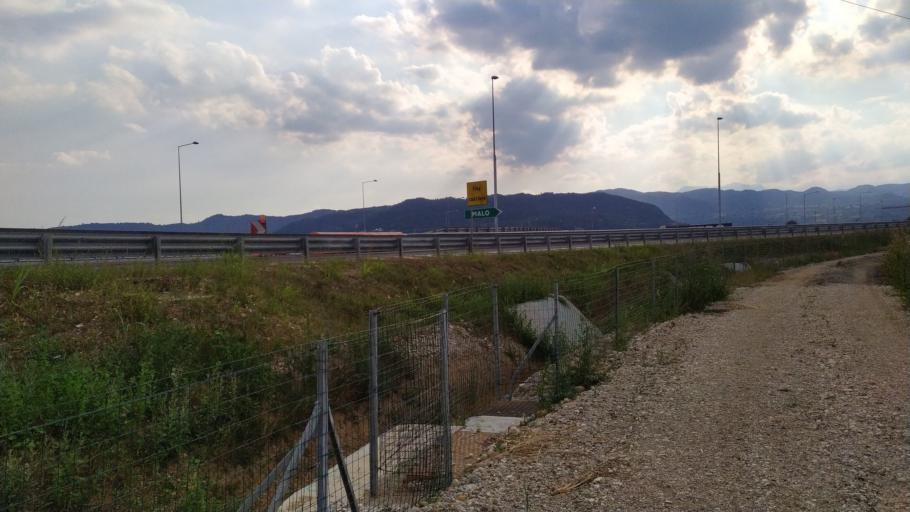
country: IT
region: Veneto
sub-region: Provincia di Vicenza
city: Isola Vicentina
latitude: 45.6491
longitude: 11.4489
